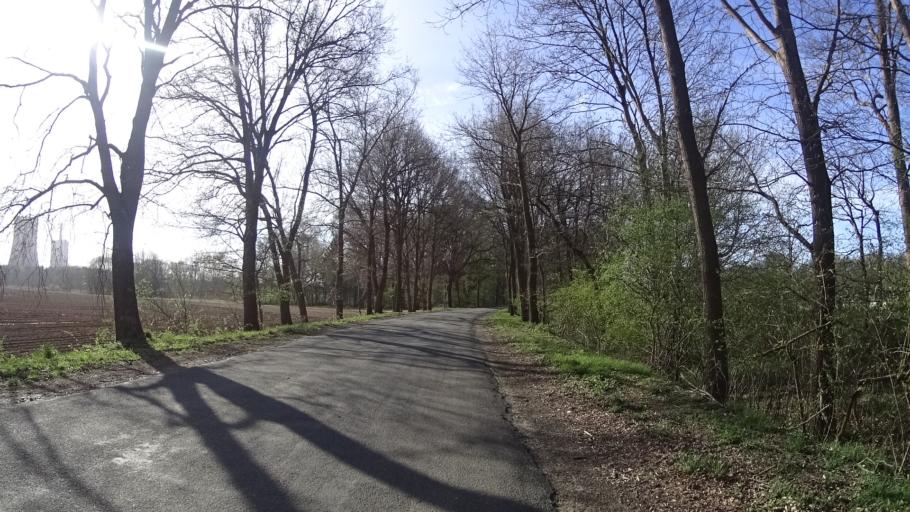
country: DE
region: Lower Saxony
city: Haren
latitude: 52.7600
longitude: 7.2583
